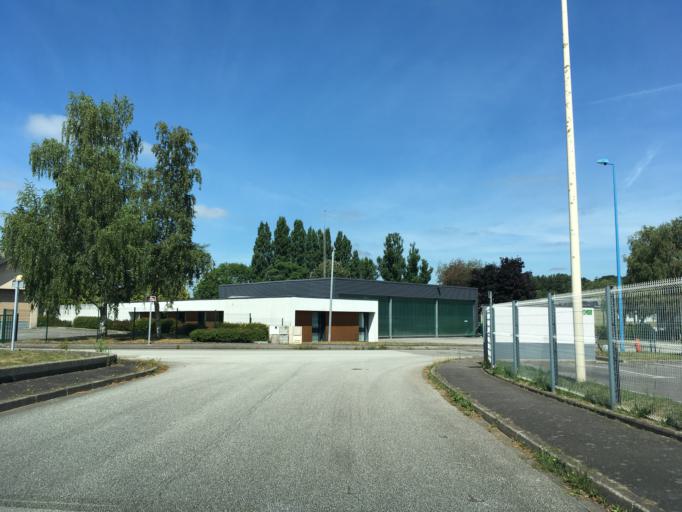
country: FR
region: Brittany
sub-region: Departement du Finistere
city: Quimper
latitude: 48.0150
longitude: -4.0916
